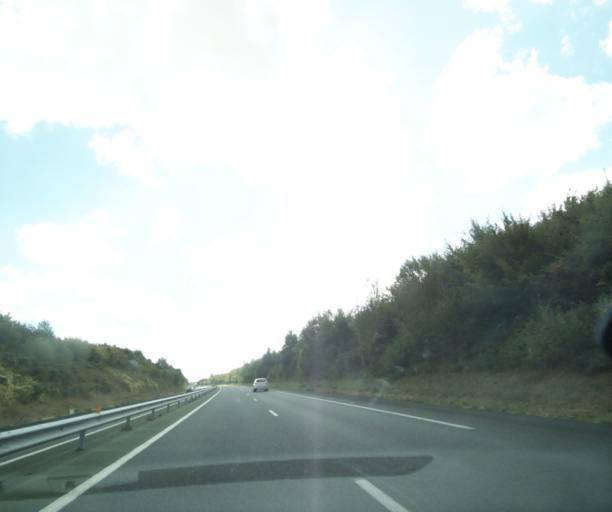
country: FR
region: Poitou-Charentes
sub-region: Departement de la Charente-Maritime
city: Saint-Georges-des-Coteaux
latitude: 45.8046
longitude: -0.6896
